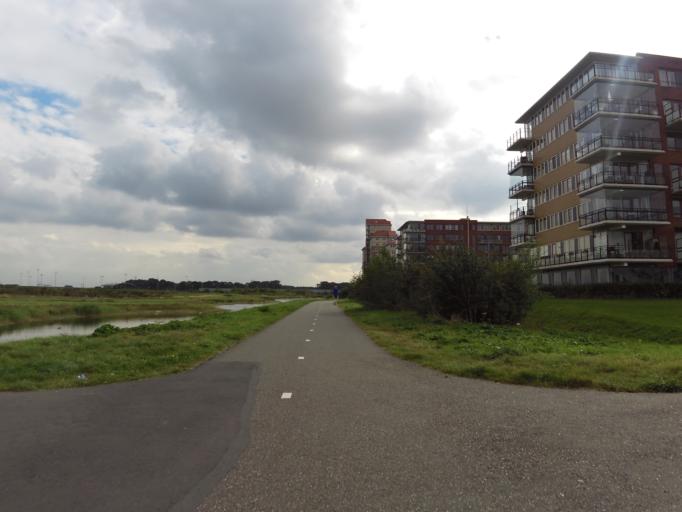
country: NL
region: South Holland
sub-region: Gemeente Rijnwoude
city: Benthuizen
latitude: 52.0668
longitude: 4.5469
